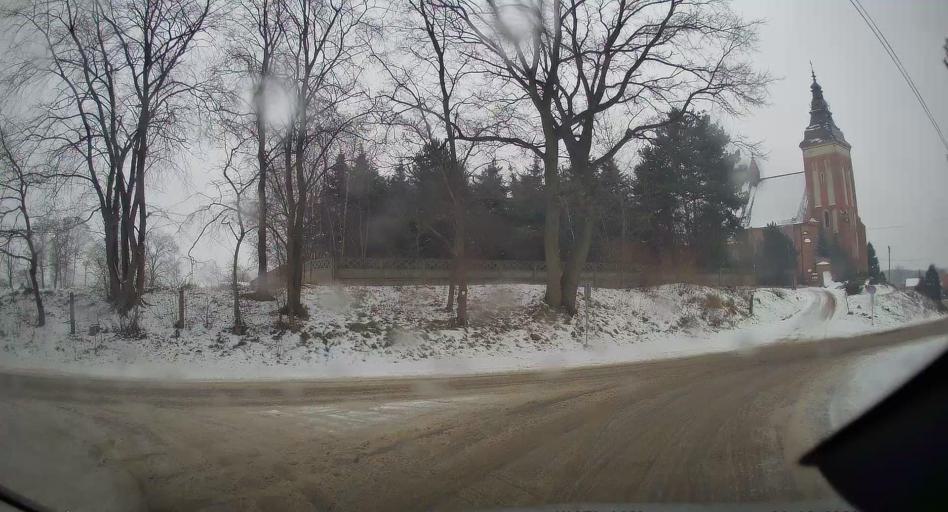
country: PL
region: Lodz Voivodeship
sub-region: Powiat tomaszowski
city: Czerniewice
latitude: 51.6774
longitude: 20.2190
